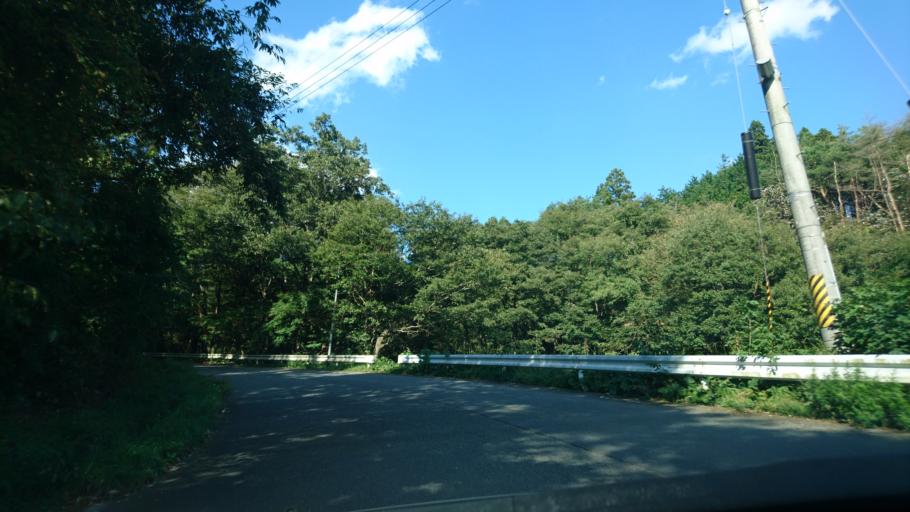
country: JP
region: Iwate
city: Ichinoseki
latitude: 38.8675
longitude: 141.0452
